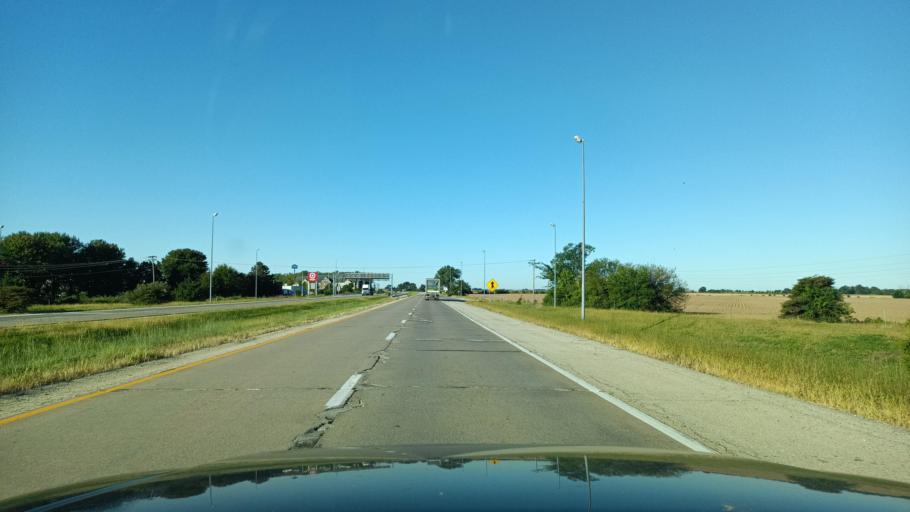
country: US
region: Illinois
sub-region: Knox County
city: Galesburg
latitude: 40.9741
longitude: -90.3937
